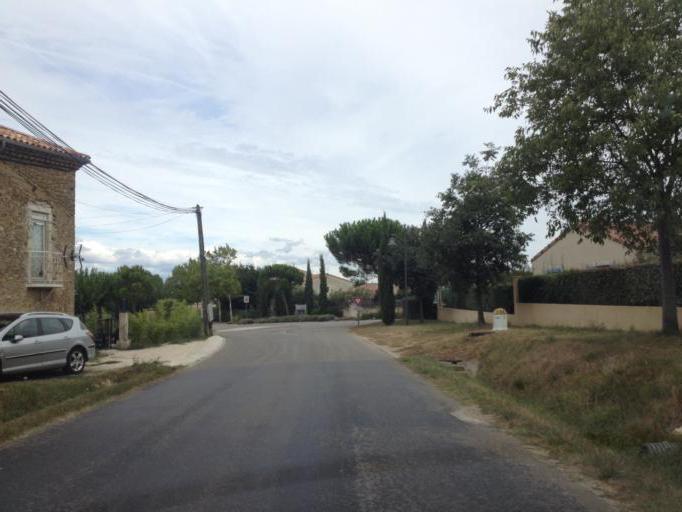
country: FR
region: Rhone-Alpes
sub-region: Departement de la Drome
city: Allan
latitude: 44.4963
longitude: 4.7887
